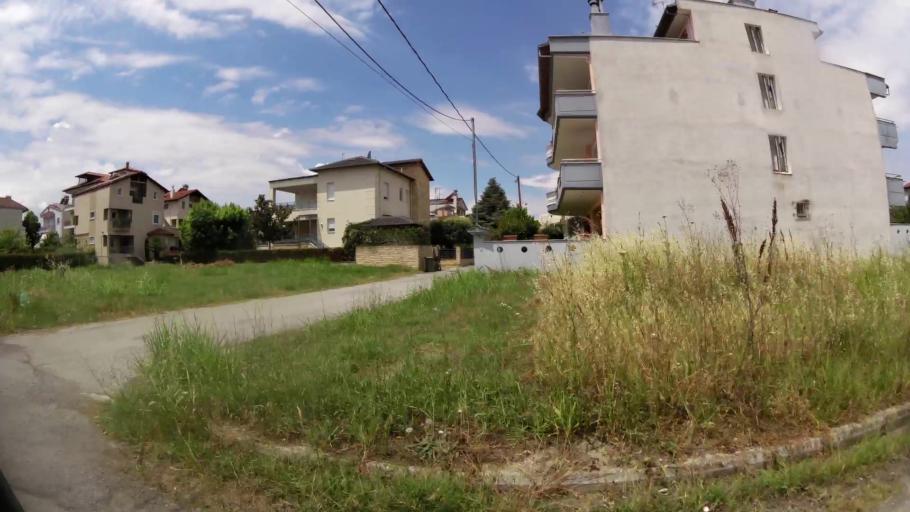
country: GR
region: Central Macedonia
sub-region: Nomos Pierias
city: Katerini
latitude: 40.2641
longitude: 22.5191
